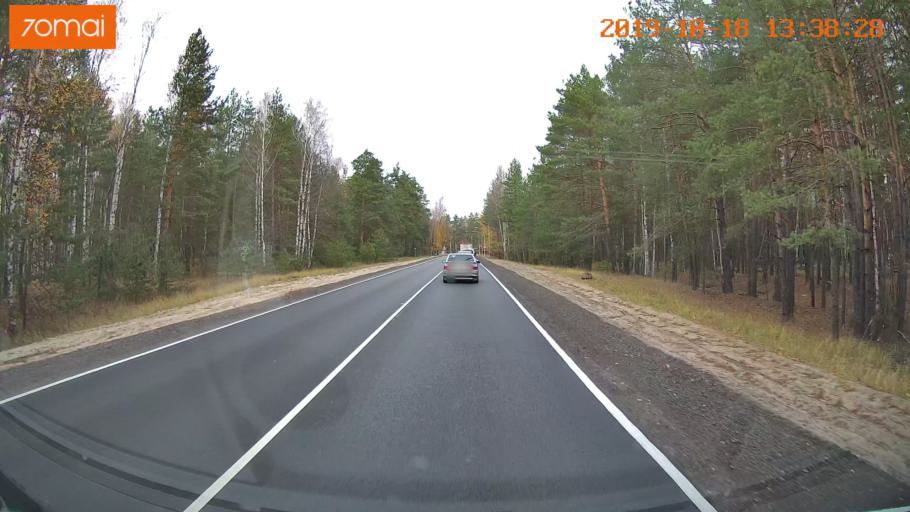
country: RU
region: Rjazan
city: Solotcha
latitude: 54.8904
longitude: 40.0027
